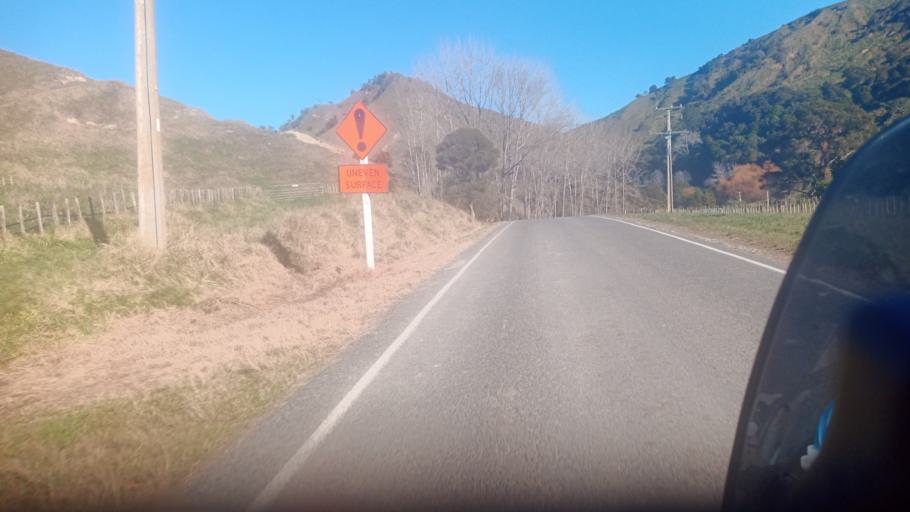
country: NZ
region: Gisborne
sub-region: Gisborne District
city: Gisborne
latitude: -38.5600
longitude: 177.6238
